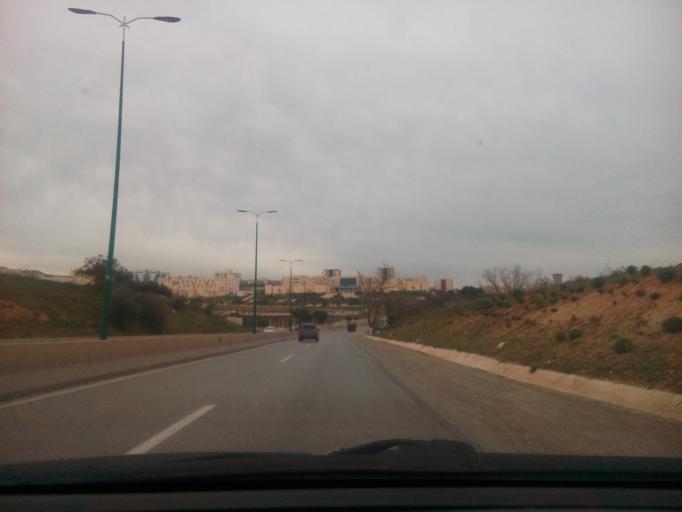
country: DZ
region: Tlemcen
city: Tlemcen
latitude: 34.9025
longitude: -1.3471
